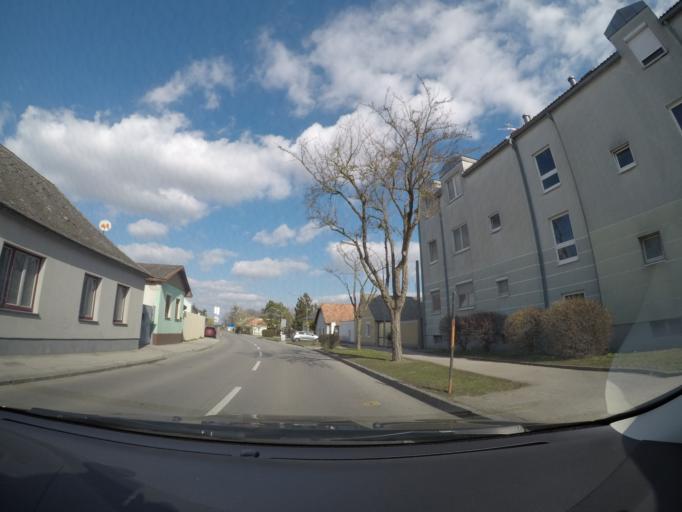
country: AT
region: Lower Austria
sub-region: Politischer Bezirk Wien-Umgebung
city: Schwadorf
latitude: 48.0736
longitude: 16.5885
